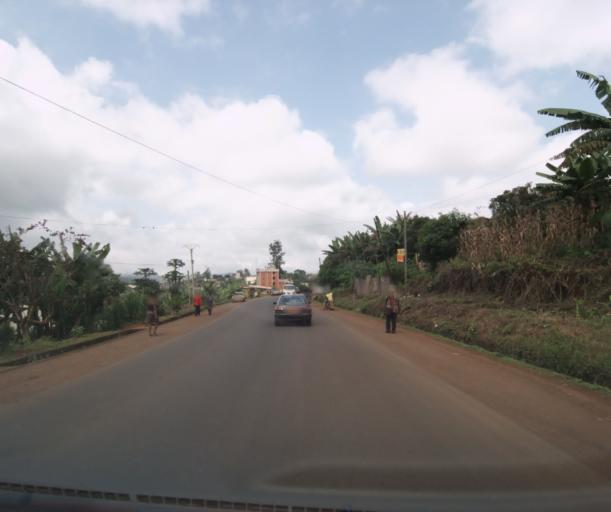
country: CM
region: West
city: Dschang
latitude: 5.4593
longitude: 10.0710
